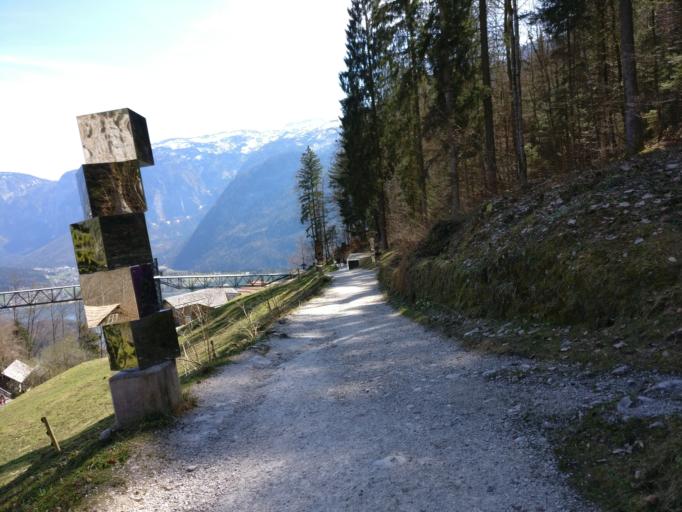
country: AT
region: Upper Austria
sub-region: Politischer Bezirk Gmunden
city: Bad Goisern
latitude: 47.5609
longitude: 13.6412
